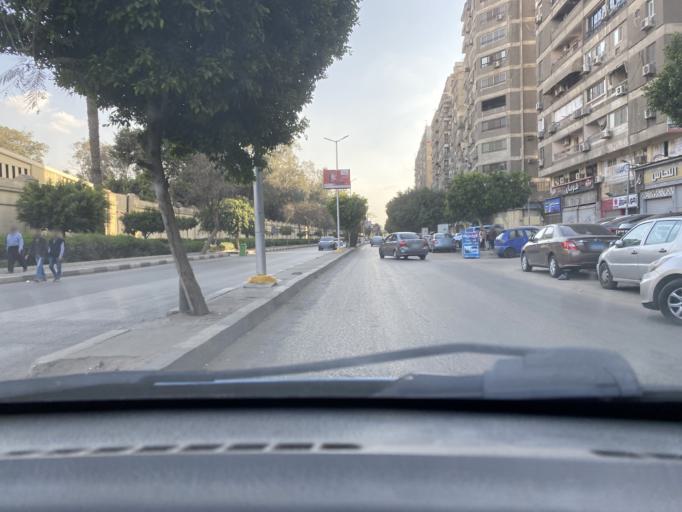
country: EG
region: Muhafazat al Qahirah
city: Cairo
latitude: 30.1021
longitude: 31.3010
